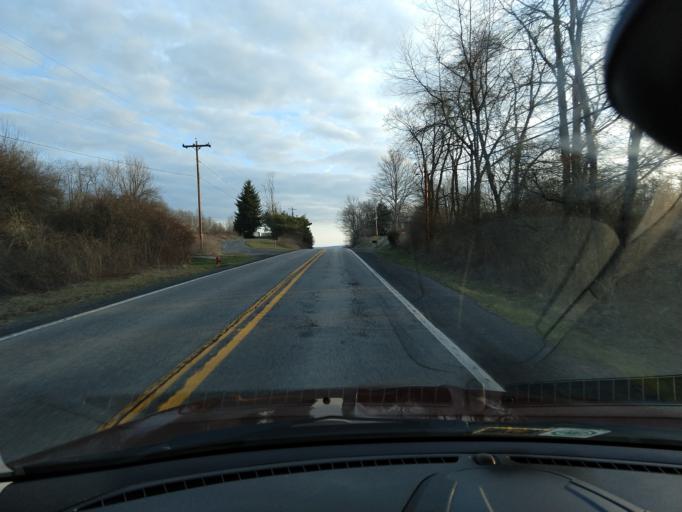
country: US
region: West Virginia
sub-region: Greenbrier County
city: Lewisburg
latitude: 37.9401
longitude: -80.3800
